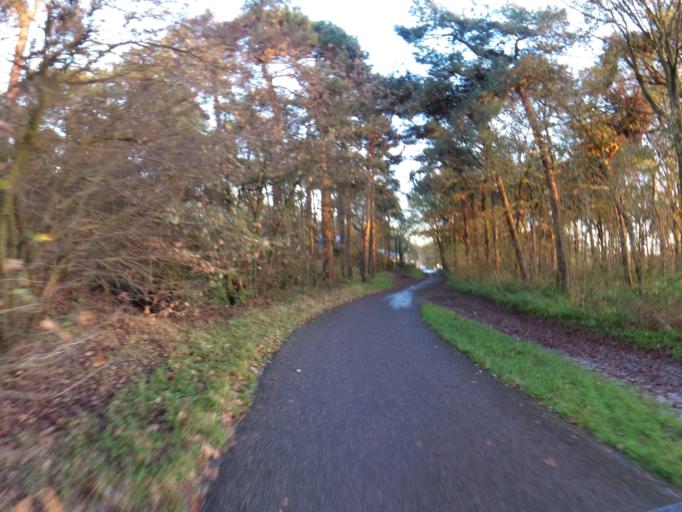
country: NL
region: North Brabant
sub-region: Gemeente Loon op Zand
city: Loon op Zand
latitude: 51.6401
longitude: 5.1468
